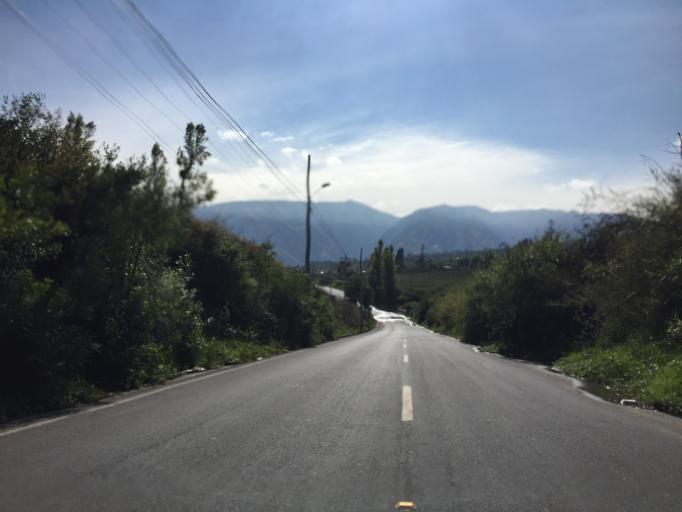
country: EC
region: Imbabura
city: Ibarra
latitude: 0.3172
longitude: -78.1511
